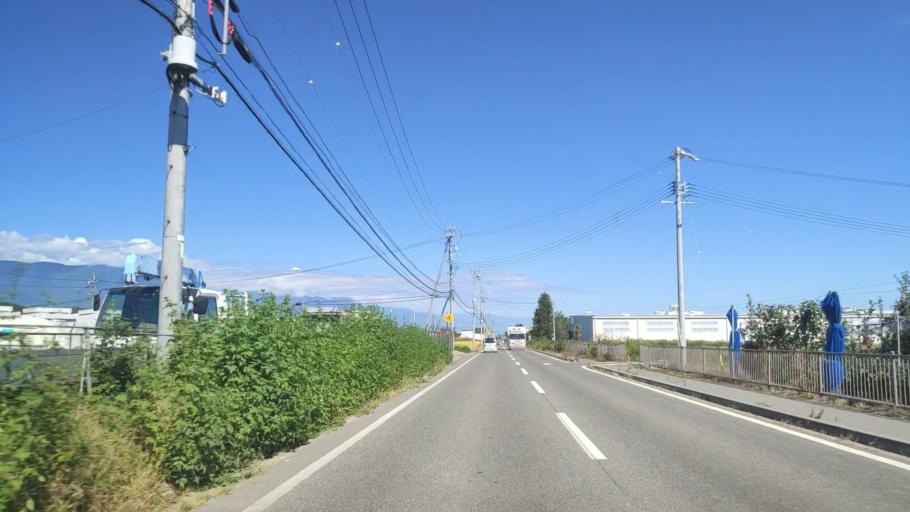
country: JP
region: Nagano
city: Matsumoto
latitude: 36.1711
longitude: 137.9152
